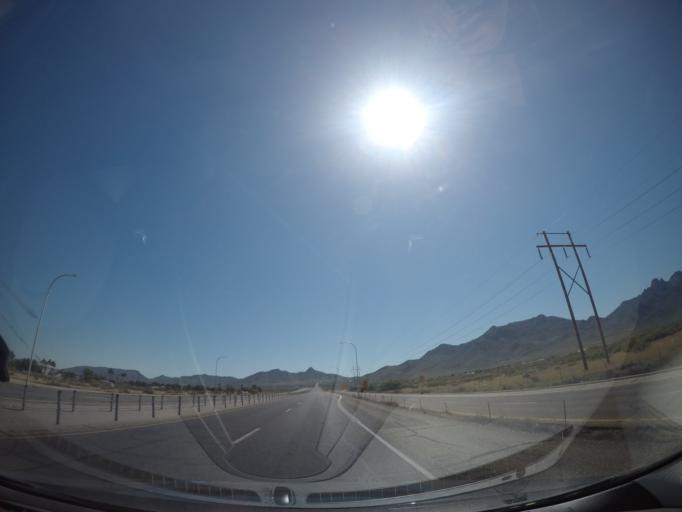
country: US
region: New Mexico
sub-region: Dona Ana County
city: White Sands
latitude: 32.4118
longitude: -106.6374
